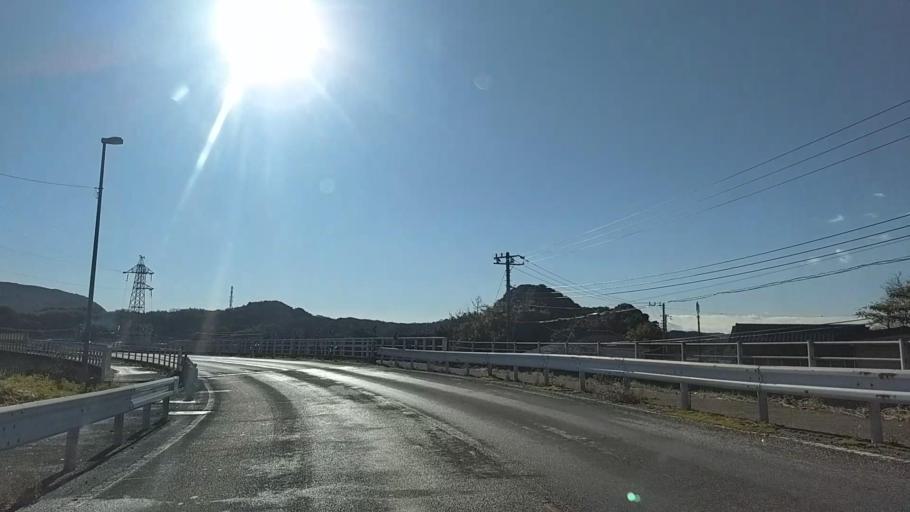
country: JP
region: Chiba
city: Kimitsu
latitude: 35.2631
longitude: 139.8745
